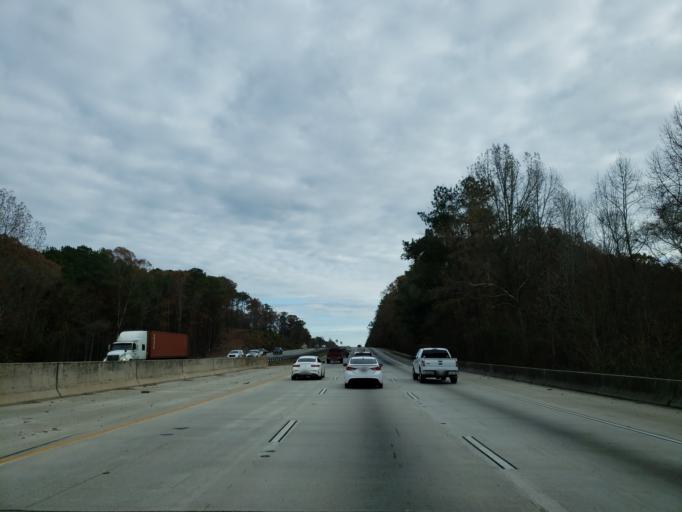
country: US
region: Georgia
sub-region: Monroe County
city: Forsyth
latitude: 33.1362
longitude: -84.0192
